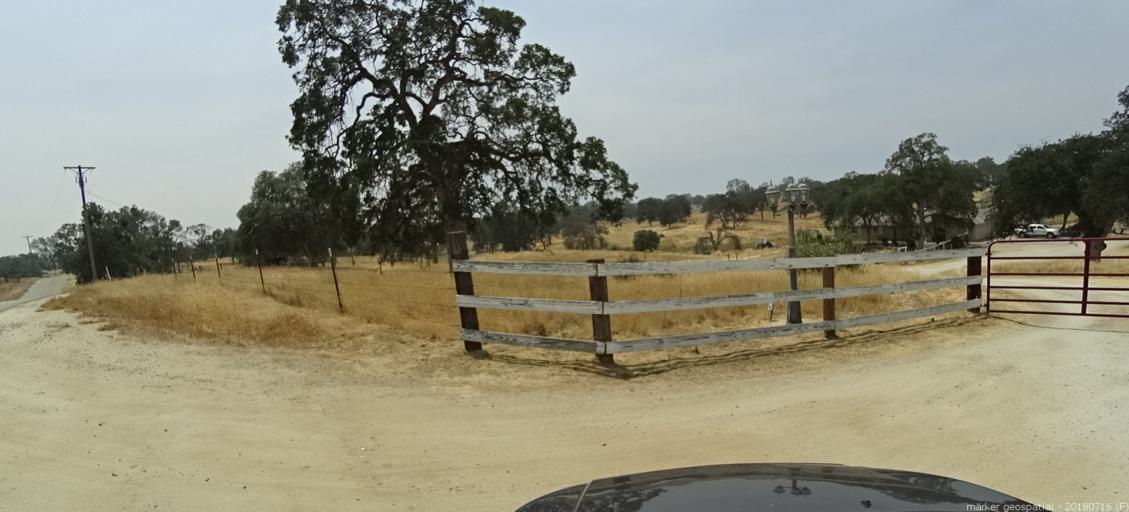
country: US
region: California
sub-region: Madera County
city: Yosemite Lakes
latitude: 37.2052
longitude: -119.9001
